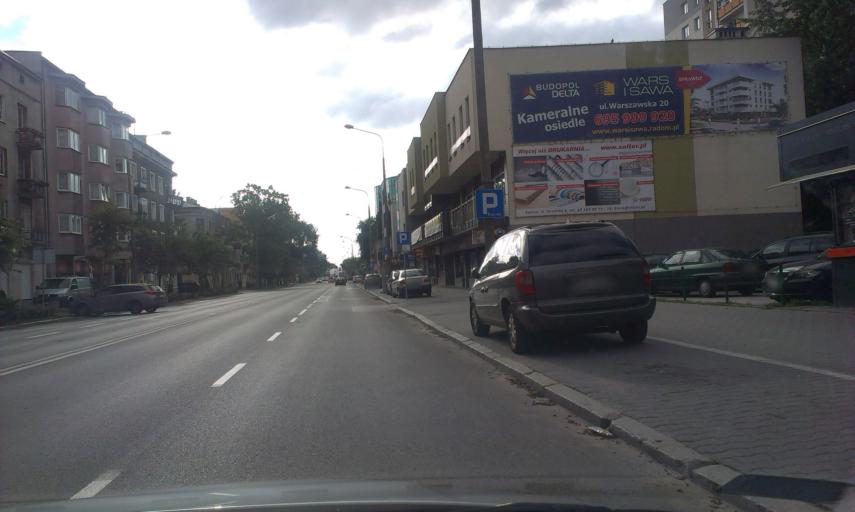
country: PL
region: Masovian Voivodeship
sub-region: Radom
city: Radom
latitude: 51.4000
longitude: 21.1636
